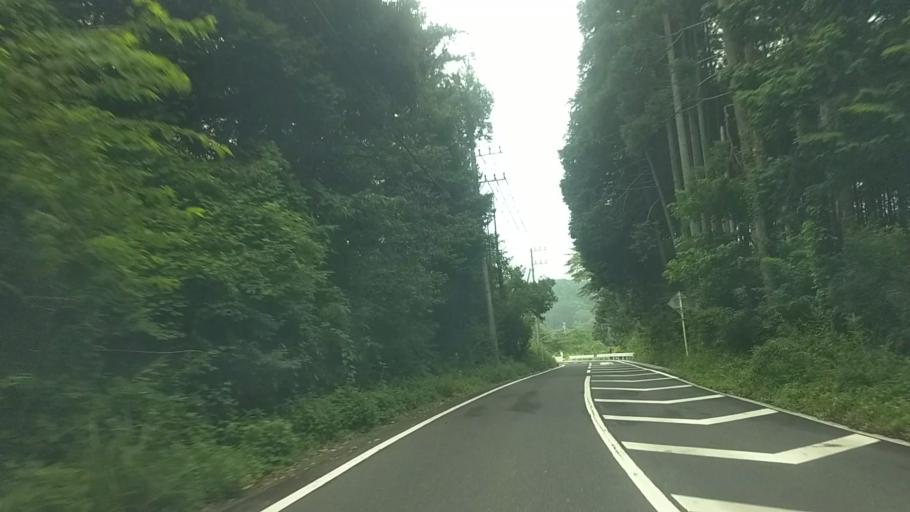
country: JP
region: Chiba
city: Kisarazu
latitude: 35.2646
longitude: 140.0489
